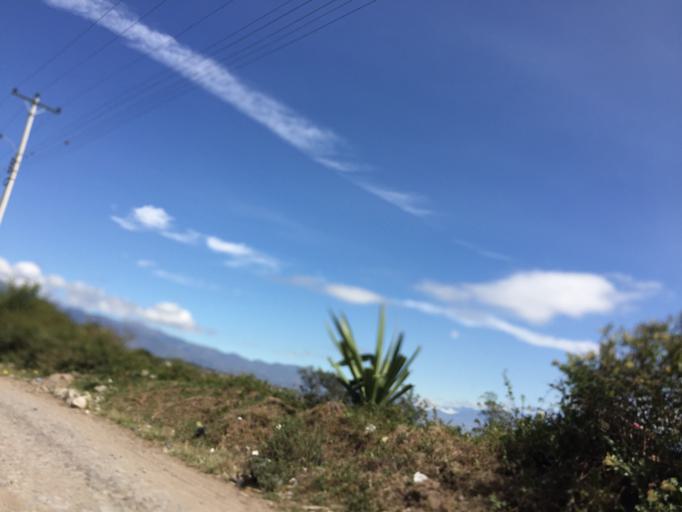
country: EC
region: Imbabura
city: Ibarra
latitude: 0.3135
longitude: -78.1560
